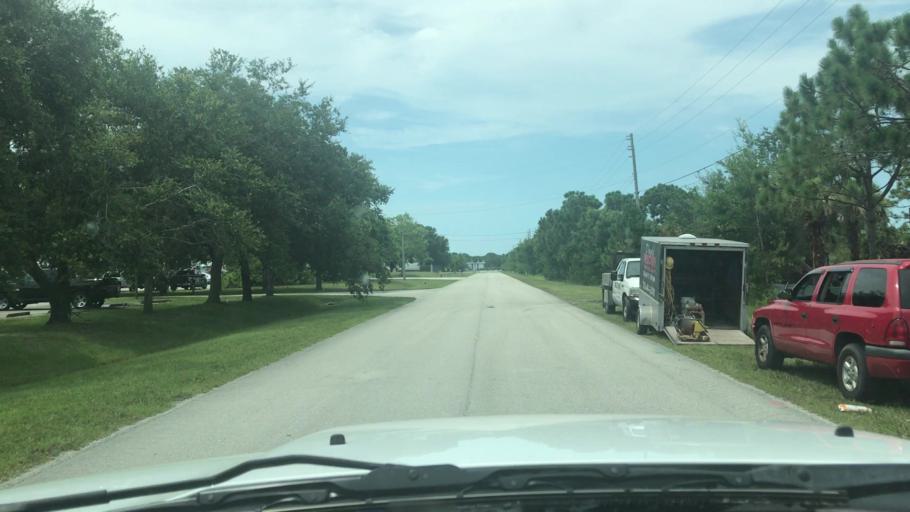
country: US
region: Florida
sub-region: Saint Lucie County
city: Fort Pierce North
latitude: 27.4888
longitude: -80.3518
